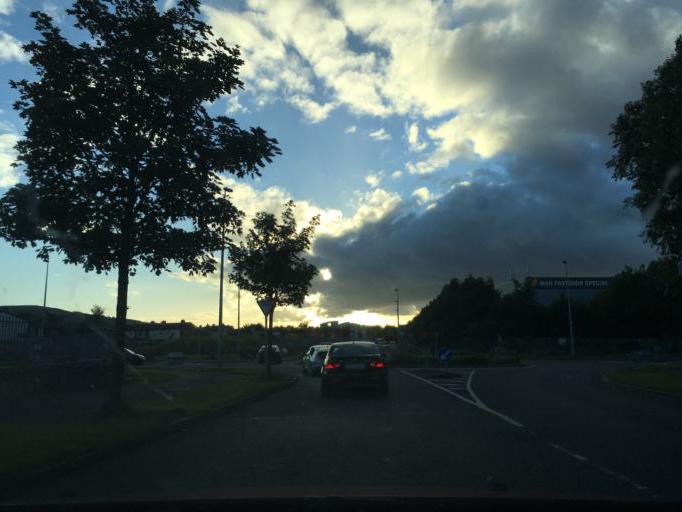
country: IE
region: Leinster
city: Oldbawn
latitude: 53.2770
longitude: -6.3729
